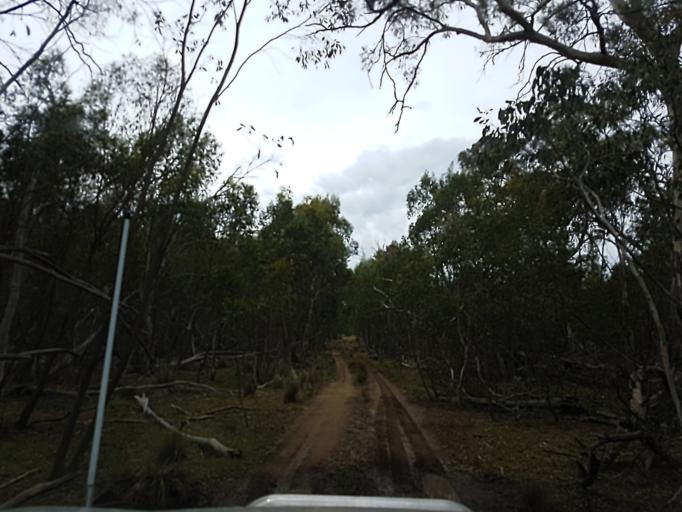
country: AU
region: New South Wales
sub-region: Snowy River
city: Jindabyne
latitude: -36.8538
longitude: 148.2604
